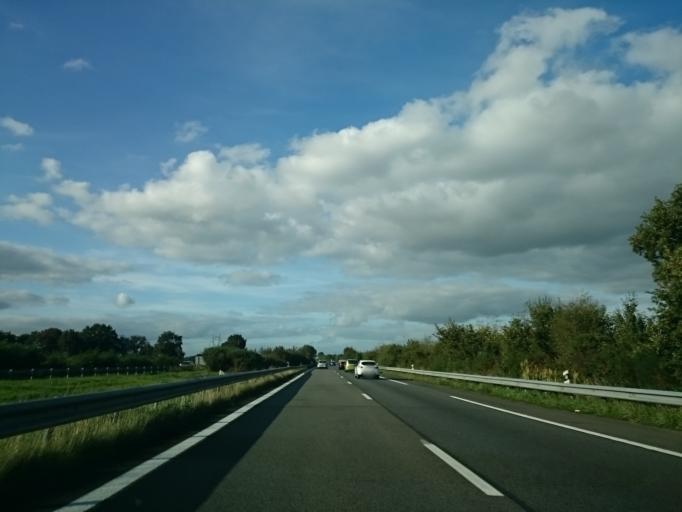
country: FR
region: Pays de la Loire
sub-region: Departement de la Loire-Atlantique
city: La Grigonnais
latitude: 47.5049
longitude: -1.6389
